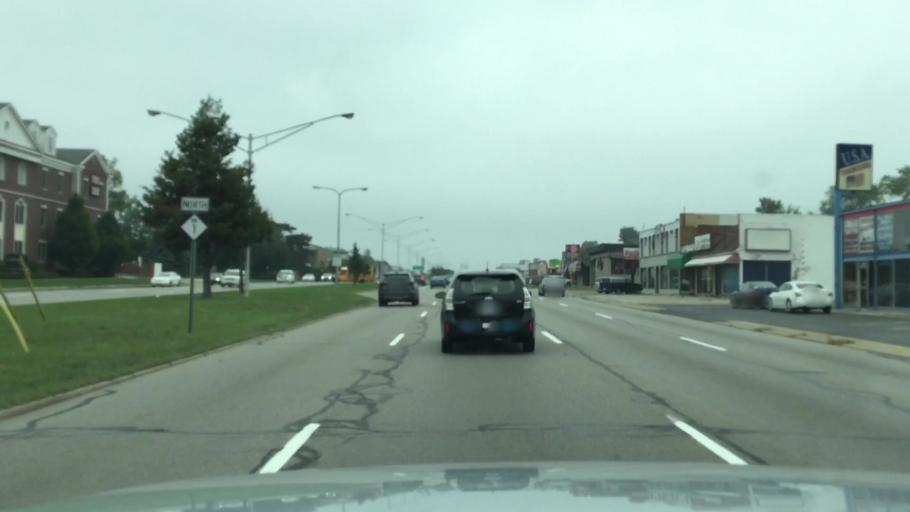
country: US
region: Michigan
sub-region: Oakland County
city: Berkley
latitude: 42.5251
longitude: -83.1930
